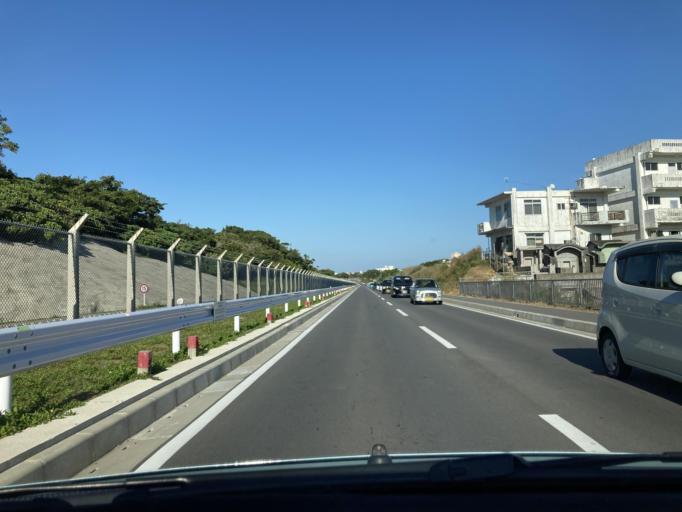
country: JP
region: Okinawa
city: Ginowan
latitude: 26.2725
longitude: 127.7668
